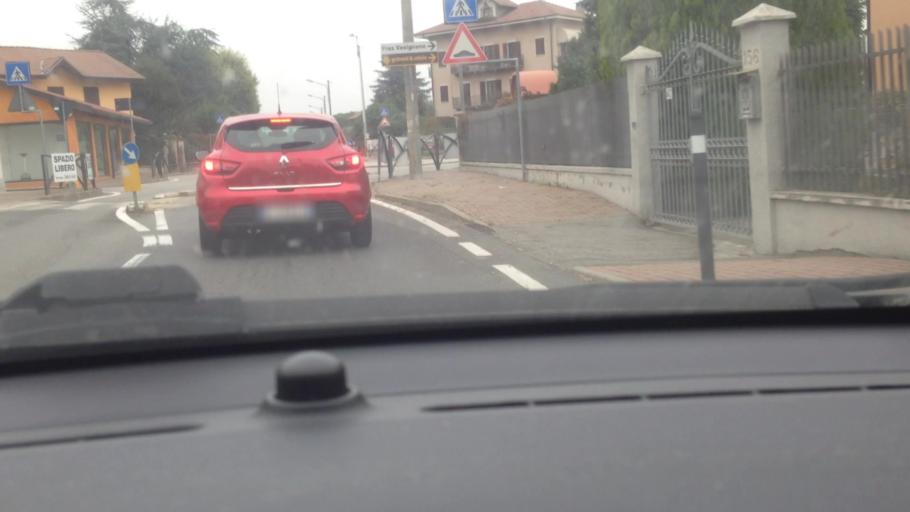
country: IT
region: Piedmont
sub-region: Provincia di Torino
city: Rivarolo Canavese
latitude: 45.3432
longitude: 7.7105
